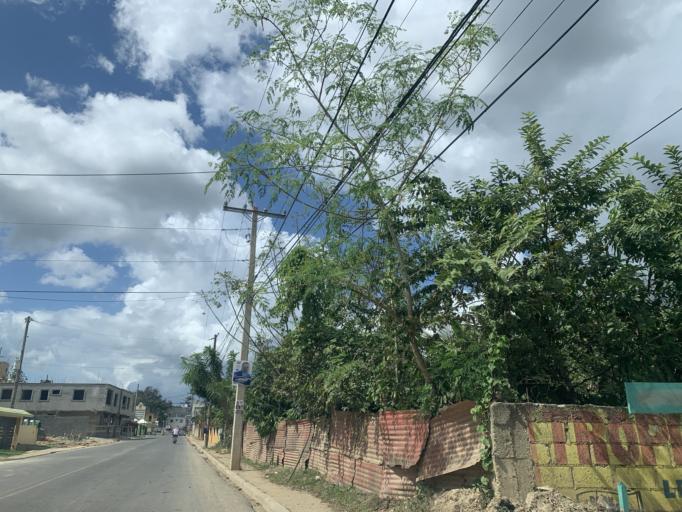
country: DO
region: Monte Plata
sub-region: Yamasa
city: Yamasa
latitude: 18.7650
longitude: -70.0201
